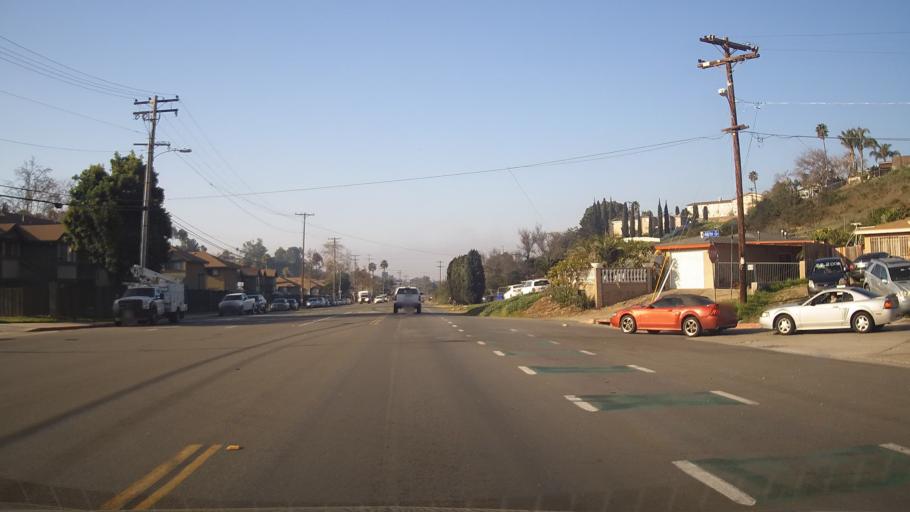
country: US
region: California
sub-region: San Diego County
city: National City
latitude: 32.7324
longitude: -117.0959
